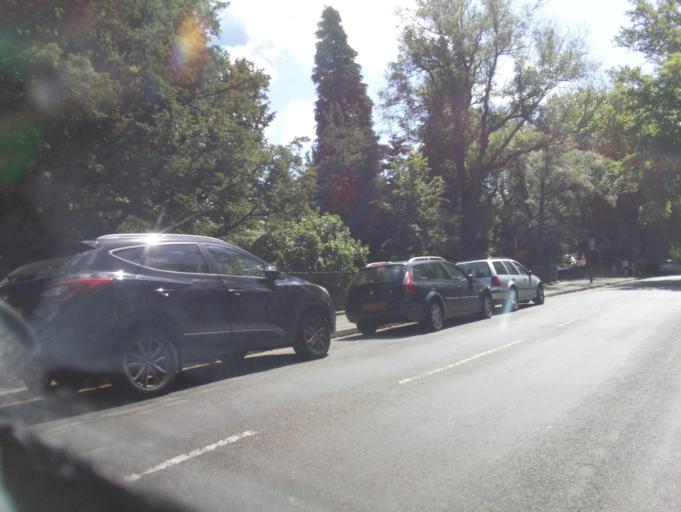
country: GB
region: England
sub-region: Derbyshire
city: Buxton
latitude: 53.2568
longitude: -1.9208
